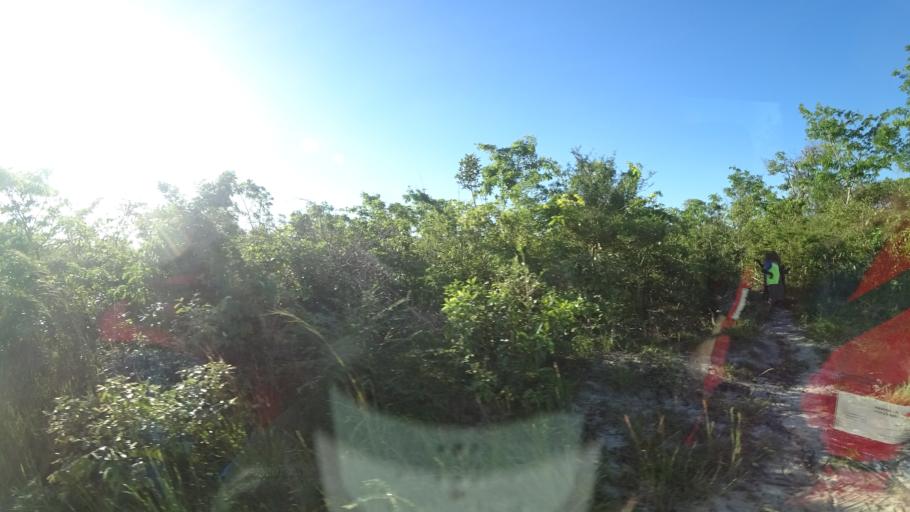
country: MZ
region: Sofala
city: Beira
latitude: -19.5749
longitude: 35.2233
